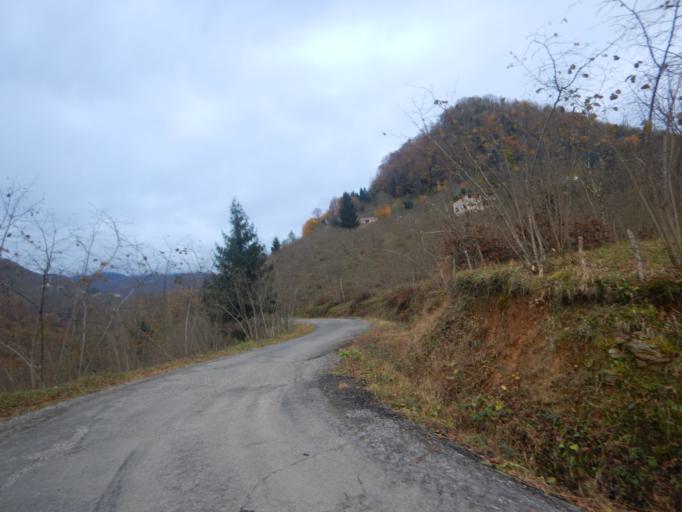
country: TR
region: Ordu
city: Kabaduz
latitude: 40.8731
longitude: 37.9187
